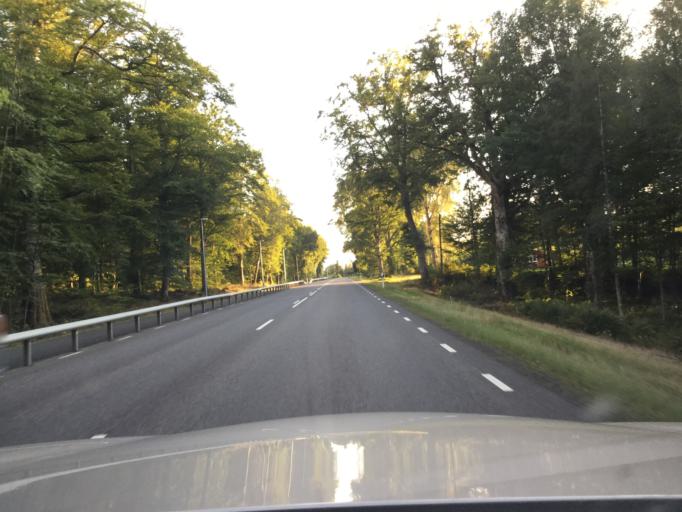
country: SE
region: Kronoberg
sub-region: Almhults Kommun
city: AElmhult
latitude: 56.6630
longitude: 14.2561
